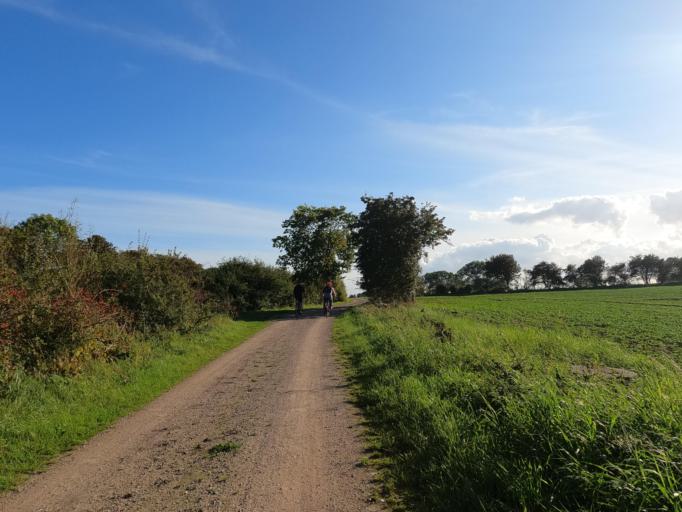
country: DE
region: Schleswig-Holstein
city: Neukirchen
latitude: 54.3501
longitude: 11.0447
